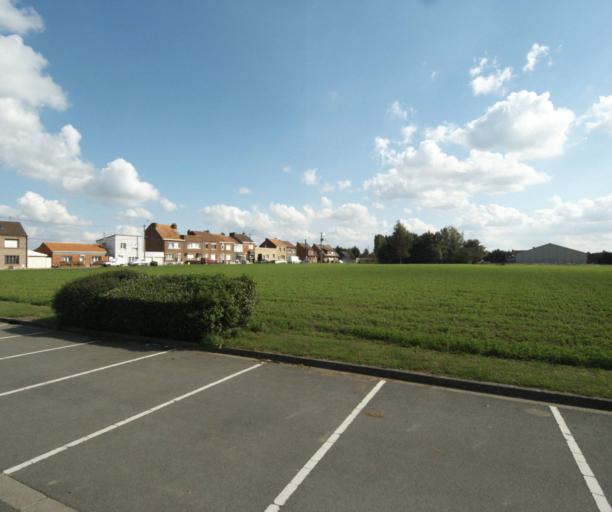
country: FR
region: Nord-Pas-de-Calais
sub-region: Departement du Nord
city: Illies
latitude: 50.5619
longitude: 2.8370
